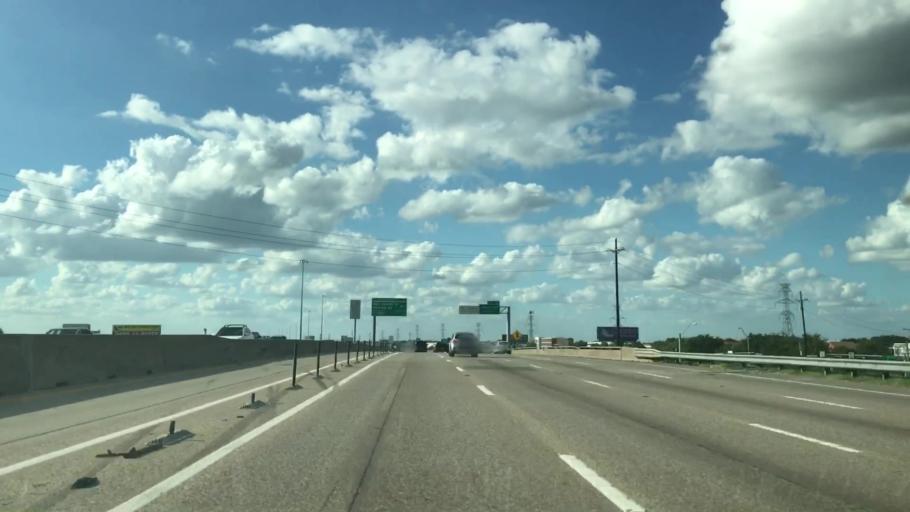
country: US
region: Texas
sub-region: Dallas County
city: Garland
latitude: 32.8744
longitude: -96.6826
